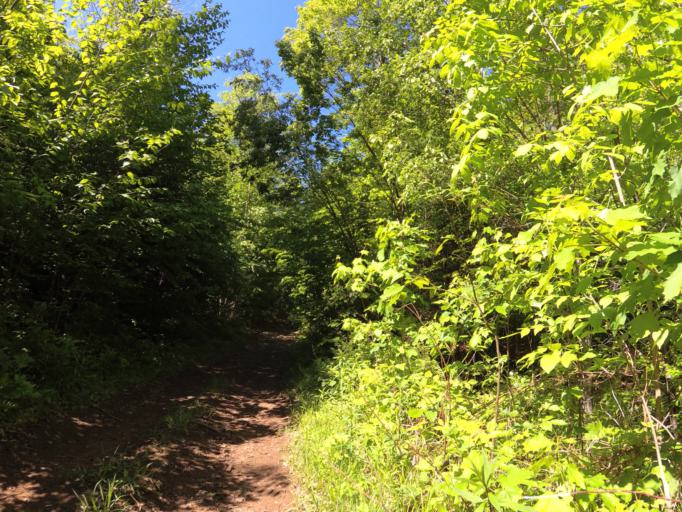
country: CA
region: Ontario
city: Renfrew
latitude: 45.0684
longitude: -77.0728
